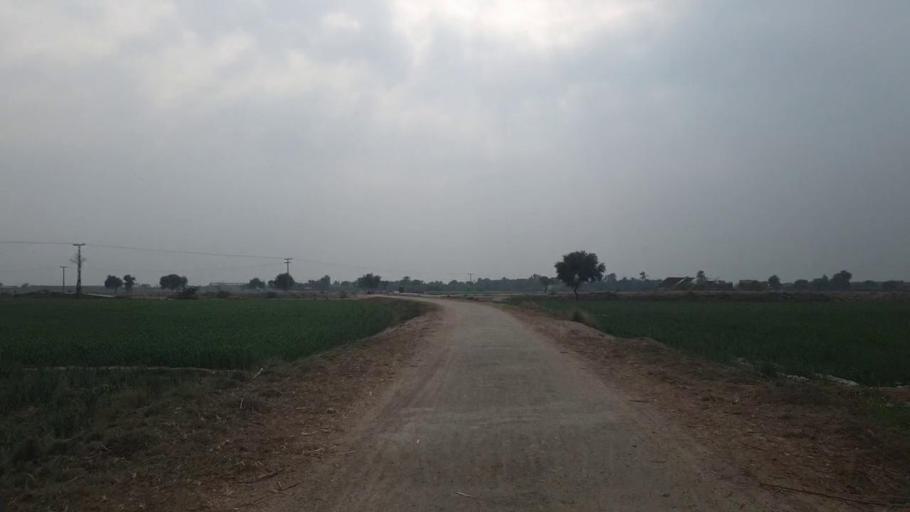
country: PK
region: Sindh
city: Shahdadpur
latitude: 25.9442
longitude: 68.7031
